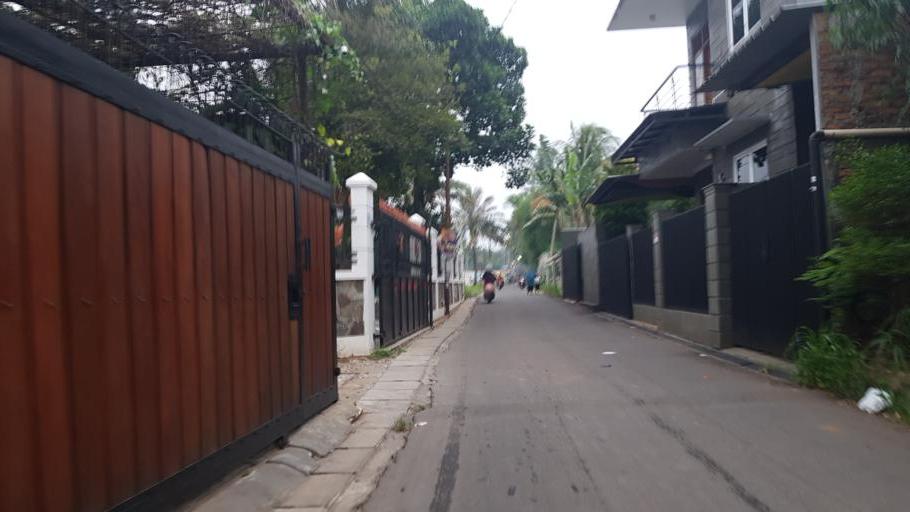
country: ID
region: West Java
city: Depok
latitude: -6.3699
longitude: 106.8019
